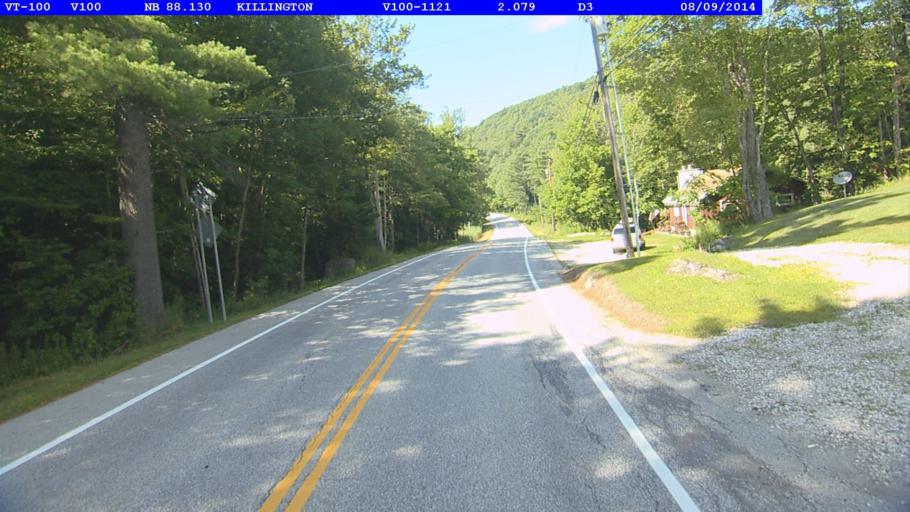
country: US
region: Vermont
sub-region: Rutland County
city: Rutland
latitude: 43.6951
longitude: -72.8142
